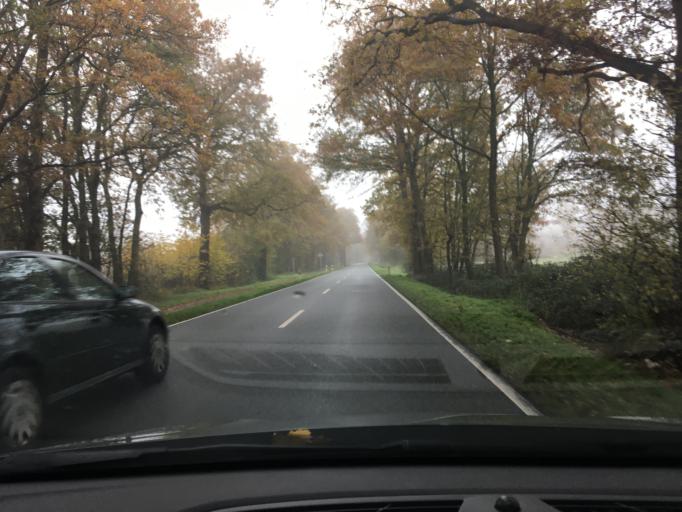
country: DE
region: North Rhine-Westphalia
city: Stadtlohn
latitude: 52.0887
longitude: 6.9144
